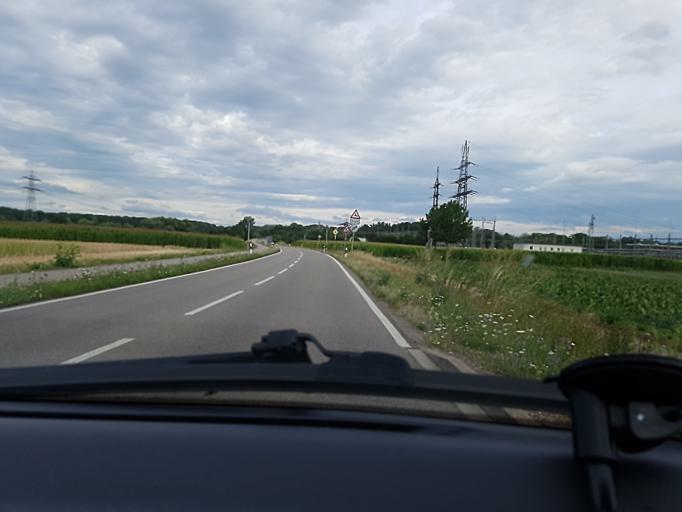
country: DE
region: Baden-Wuerttemberg
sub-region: Freiburg Region
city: Offenburg
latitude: 48.4998
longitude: 7.9139
